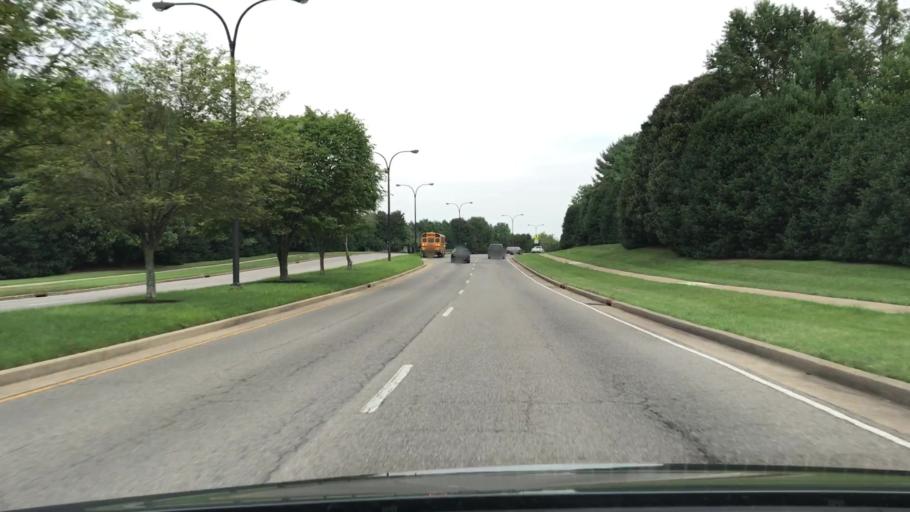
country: US
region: Tennessee
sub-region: Williamson County
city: Franklin
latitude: 35.9417
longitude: -86.7989
